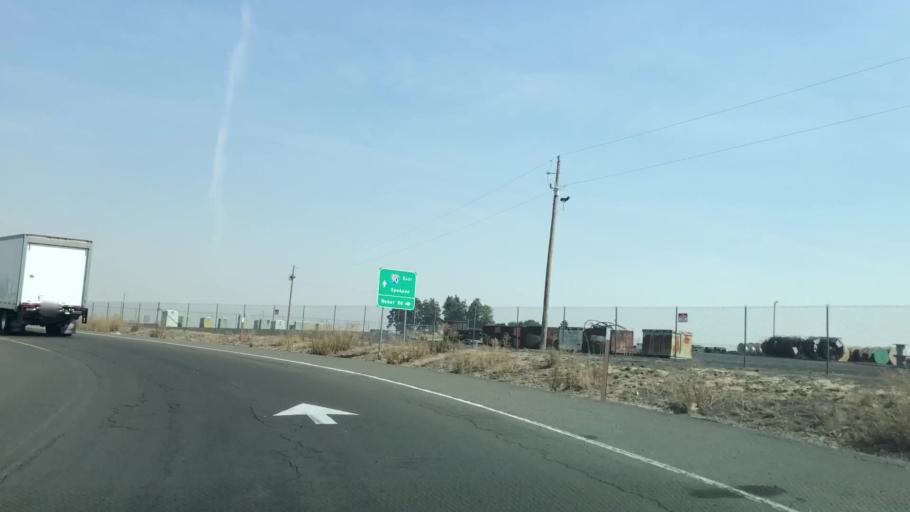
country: US
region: Washington
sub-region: Adams County
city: Ritzville
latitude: 47.1151
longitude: -118.3647
